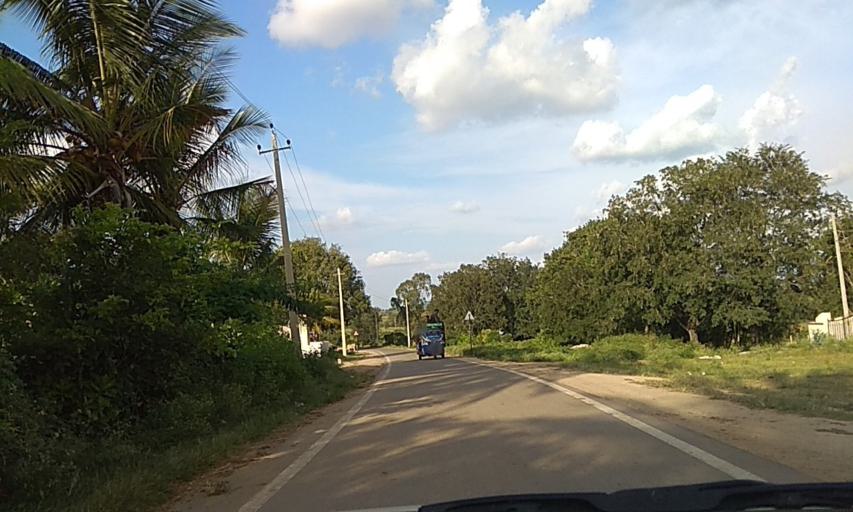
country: IN
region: Karnataka
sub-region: Chamrajnagar
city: Gundlupet
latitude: 11.7720
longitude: 76.7844
